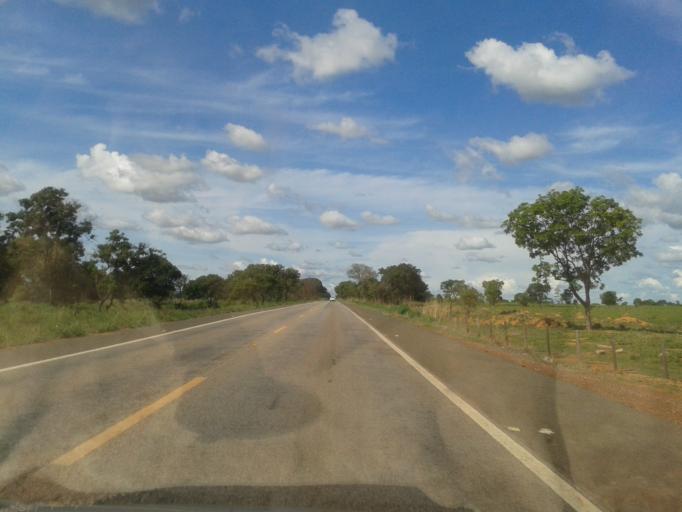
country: BR
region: Goias
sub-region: Mozarlandia
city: Mozarlandia
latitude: -15.0576
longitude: -50.6124
